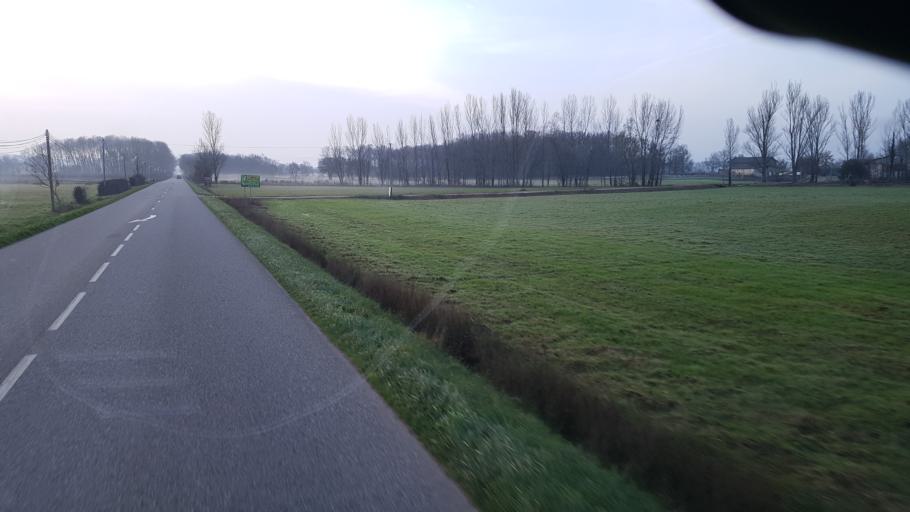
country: FR
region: Midi-Pyrenees
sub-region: Departement du Tarn-et-Garonne
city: Montricoux
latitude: 44.0971
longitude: 1.6035
